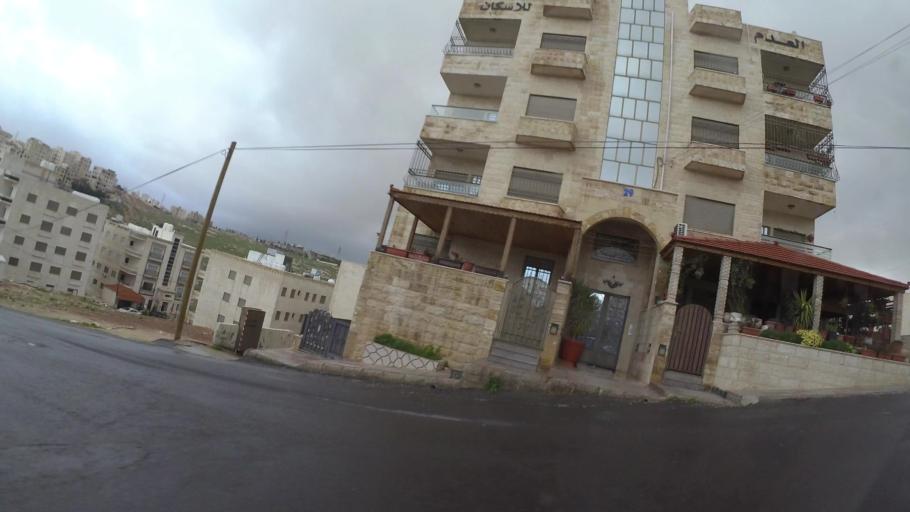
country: JO
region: Amman
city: Amman
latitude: 32.0063
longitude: 35.9296
